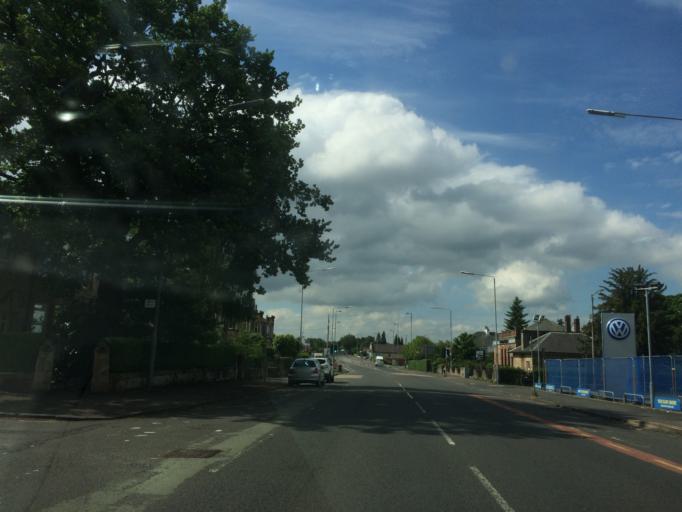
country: GB
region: Scotland
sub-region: East Renfrewshire
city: Giffnock
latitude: 55.8142
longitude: -4.2906
